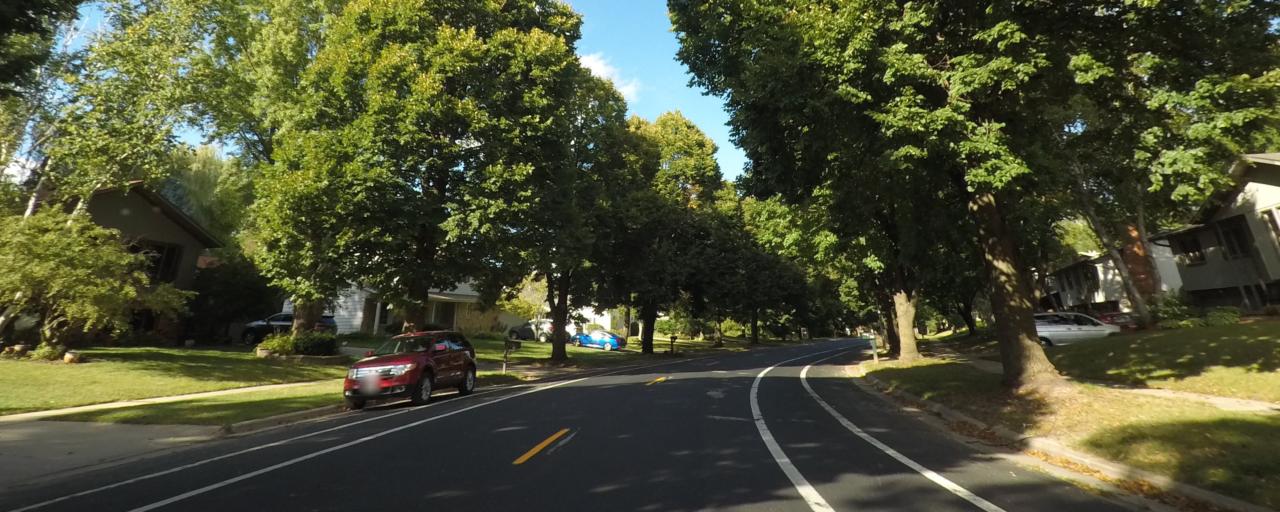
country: US
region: Wisconsin
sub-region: Dane County
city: Middleton
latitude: 43.0730
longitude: -89.5104
